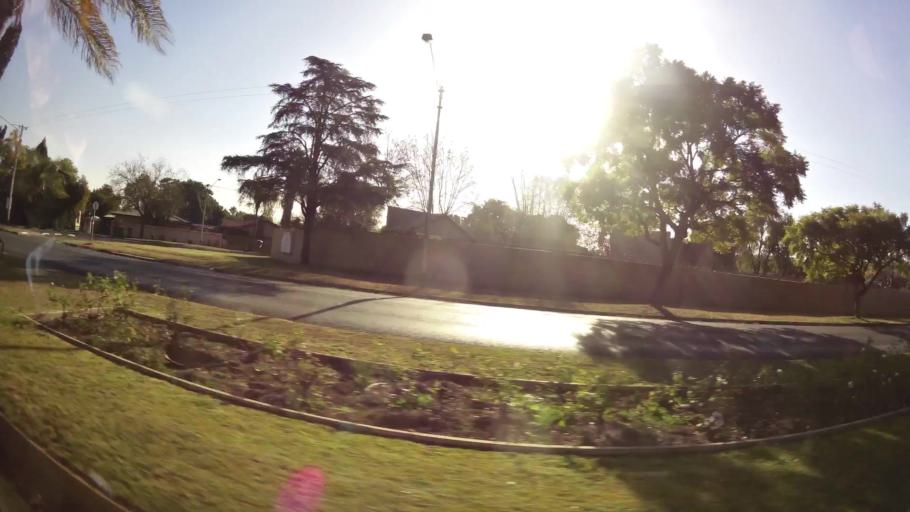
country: ZA
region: Gauteng
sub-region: City of Tshwane Metropolitan Municipality
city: Pretoria
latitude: -25.7105
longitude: 28.2258
